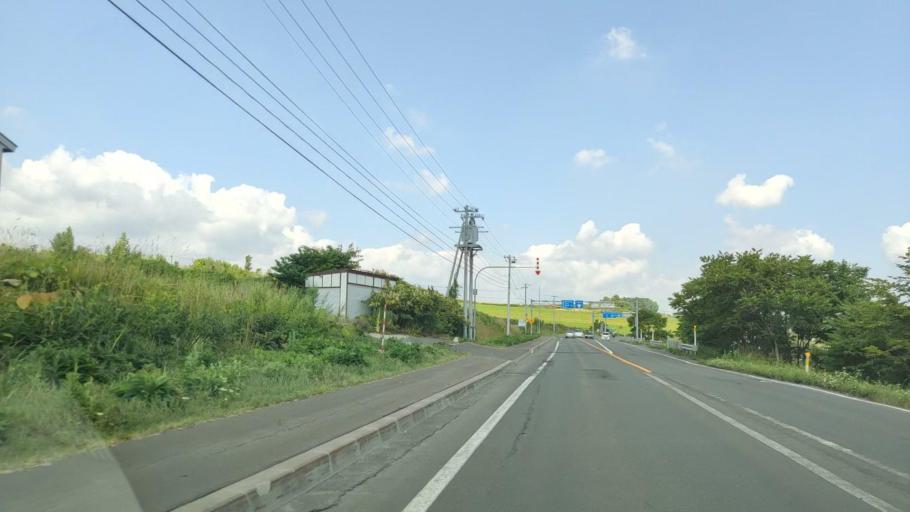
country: JP
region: Hokkaido
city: Shimo-furano
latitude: 43.5317
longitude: 142.4425
